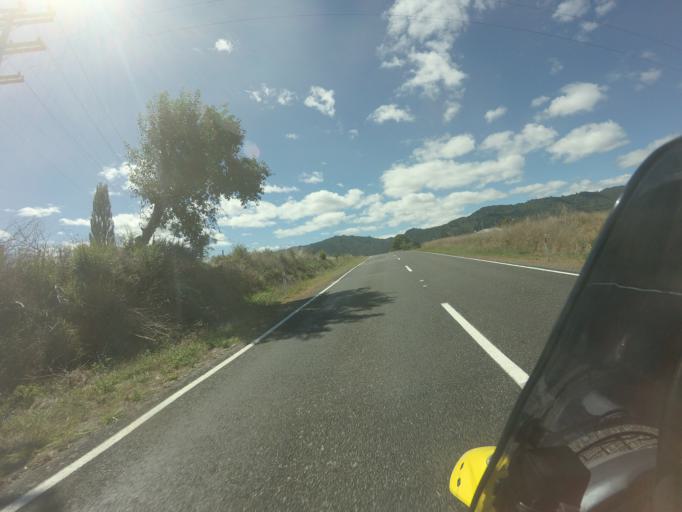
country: NZ
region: Bay of Plenty
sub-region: Kawerau District
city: Kawerau
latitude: -38.2387
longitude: 176.8305
